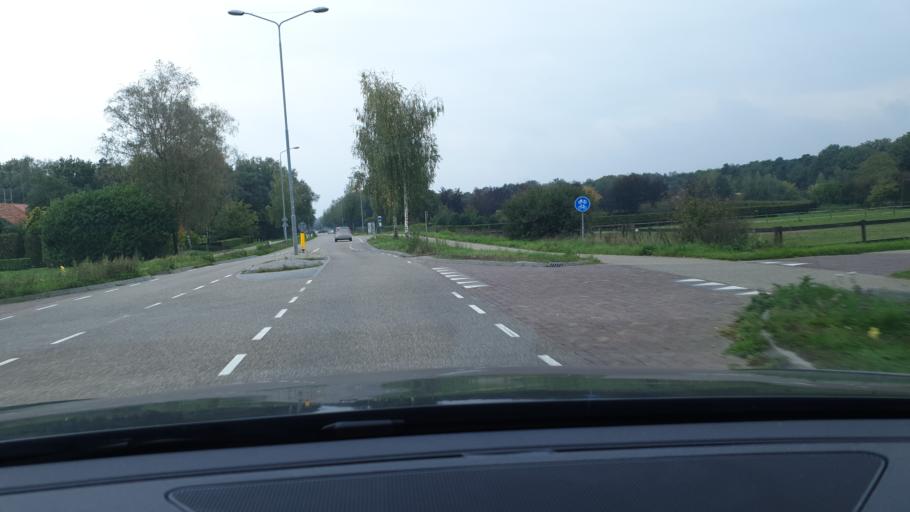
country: NL
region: North Brabant
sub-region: Gemeente Eersel
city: Eersel
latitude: 51.3708
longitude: 5.3355
